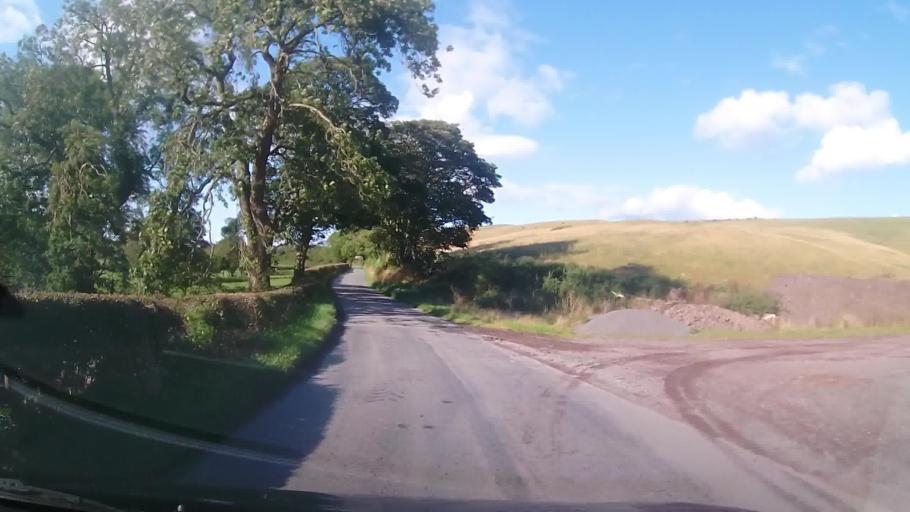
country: GB
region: England
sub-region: Shropshire
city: Pontesbury
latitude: 52.5816
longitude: -2.8818
